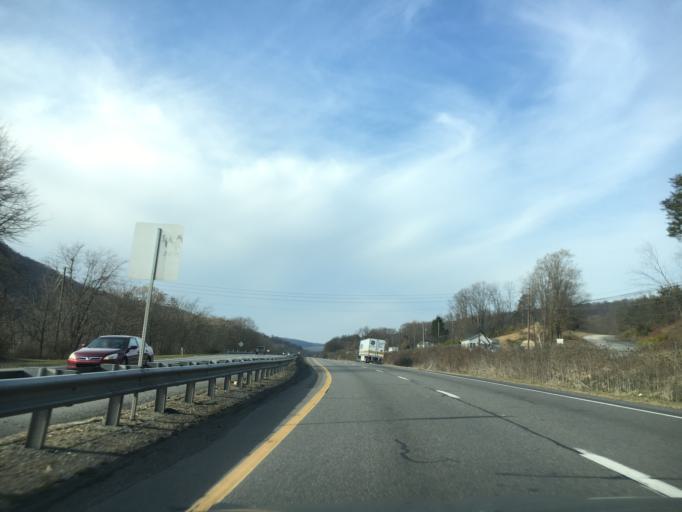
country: US
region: Pennsylvania
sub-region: Montour County
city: Danville
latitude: 40.9726
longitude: -76.6172
